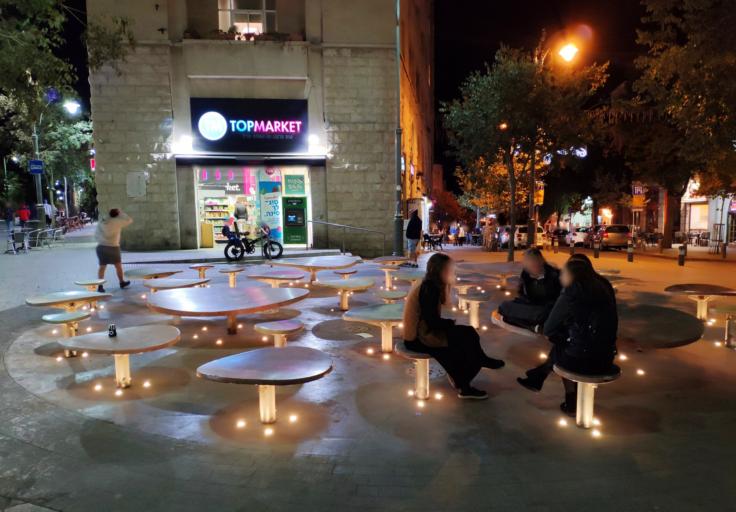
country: IL
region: Jerusalem
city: West Jerusalem
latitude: 31.7807
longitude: 35.2214
